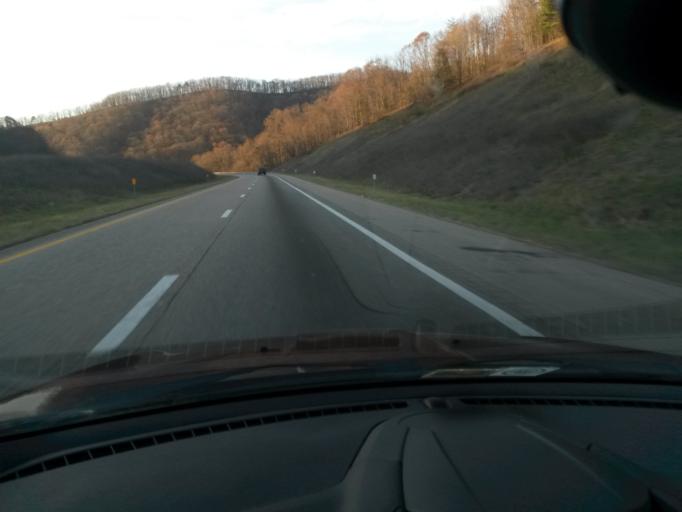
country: US
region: Virginia
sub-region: City of Lexington
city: Lexington
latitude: 37.8946
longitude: -79.5670
